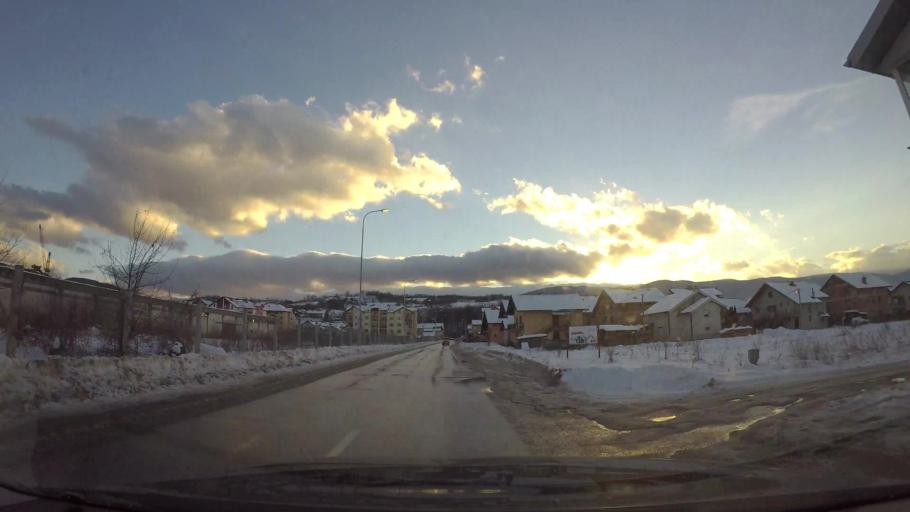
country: BA
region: Federation of Bosnia and Herzegovina
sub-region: Kanton Sarajevo
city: Sarajevo
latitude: 43.8122
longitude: 18.3632
